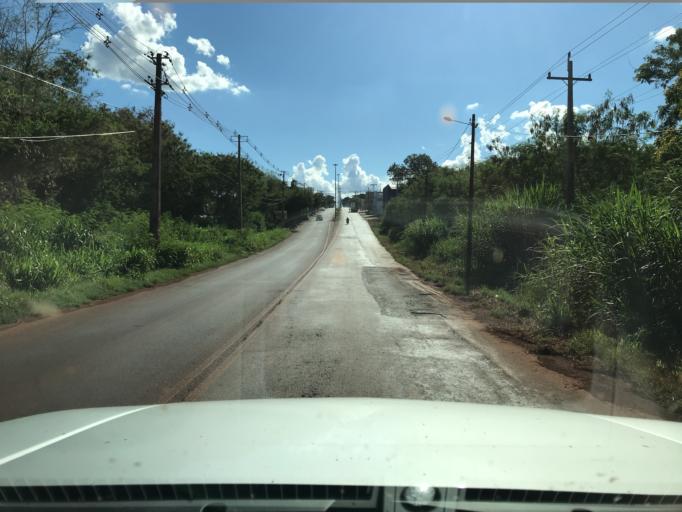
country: BR
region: Parana
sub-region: Palotina
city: Palotina
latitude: -24.2782
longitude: -53.8217
